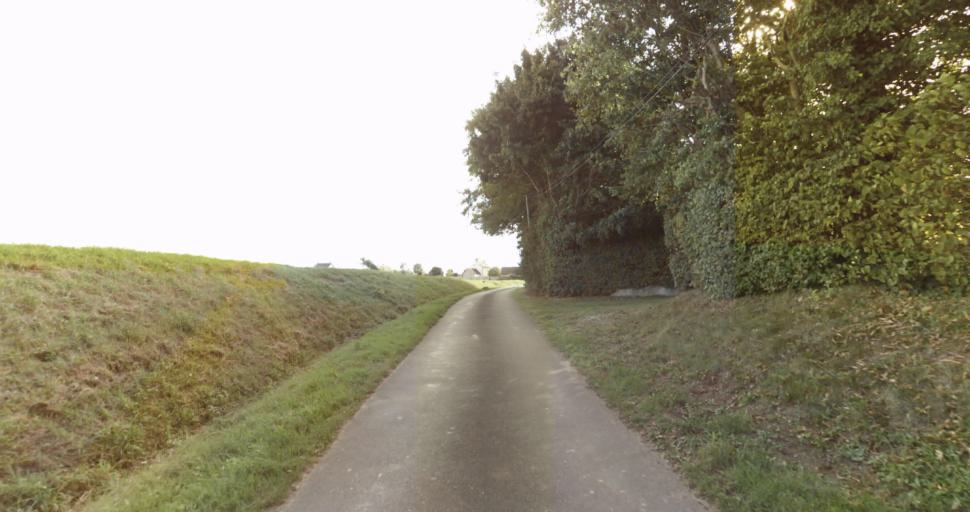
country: FR
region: Lower Normandy
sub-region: Departement de l'Orne
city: Gace
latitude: 48.7151
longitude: 0.2403
